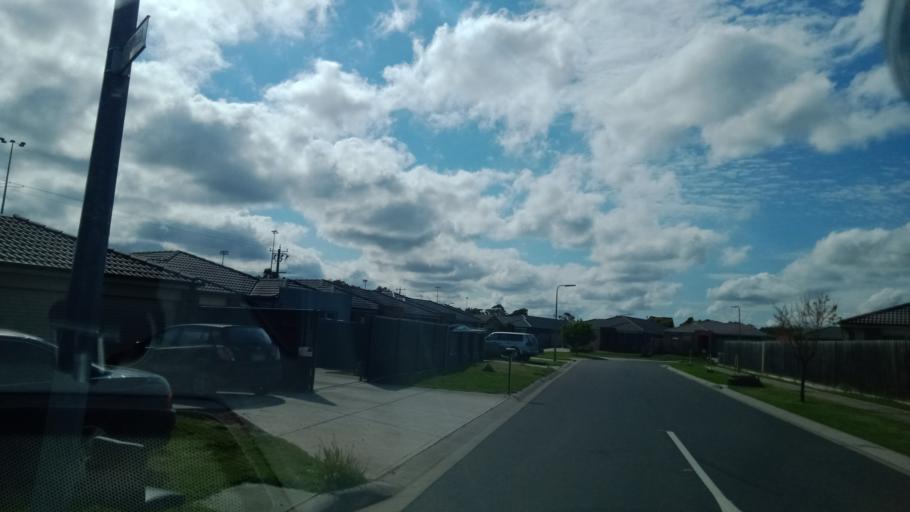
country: AU
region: Victoria
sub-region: Frankston
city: Carrum Downs
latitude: -38.0865
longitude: 145.1843
